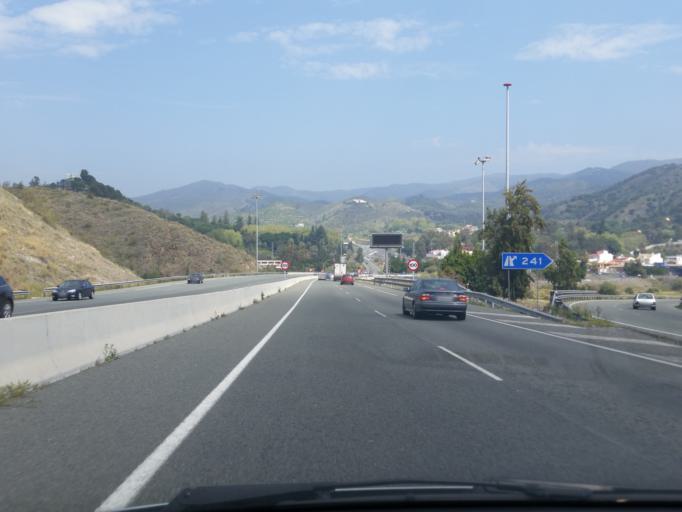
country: ES
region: Andalusia
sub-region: Provincia de Malaga
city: Malaga
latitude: 36.7532
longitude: -4.4303
